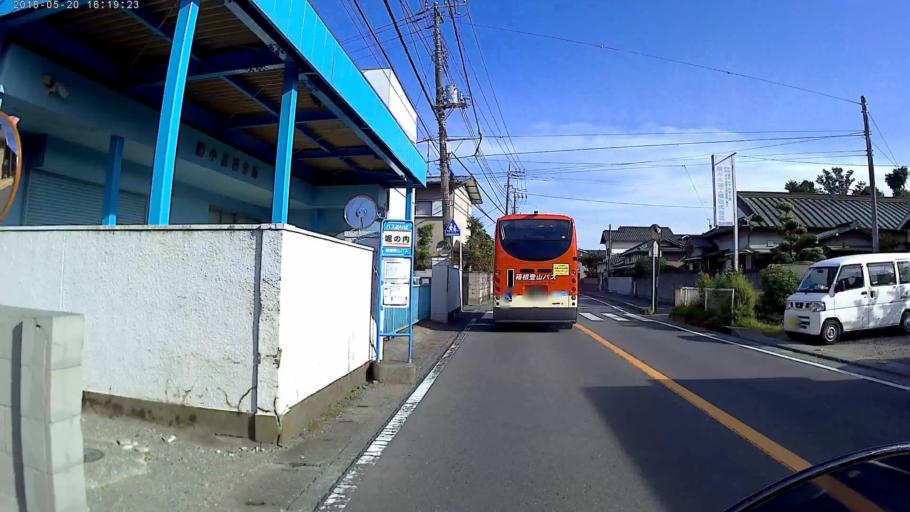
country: JP
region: Kanagawa
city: Odawara
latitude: 35.2988
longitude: 139.1470
